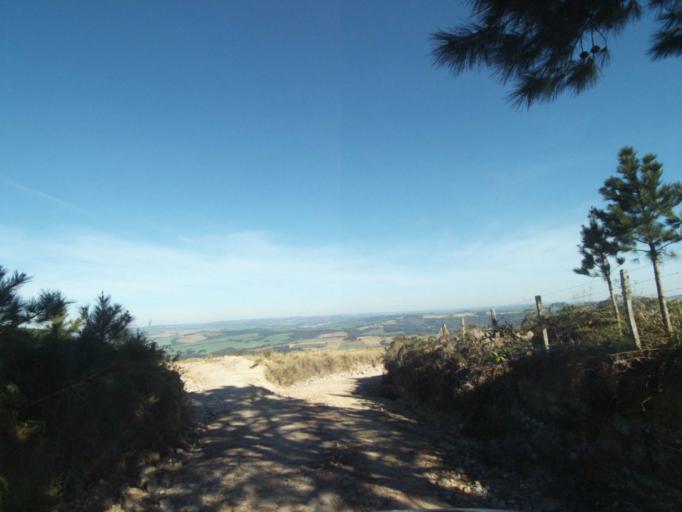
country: BR
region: Parana
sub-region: Tibagi
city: Tibagi
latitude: -24.5787
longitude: -50.4822
